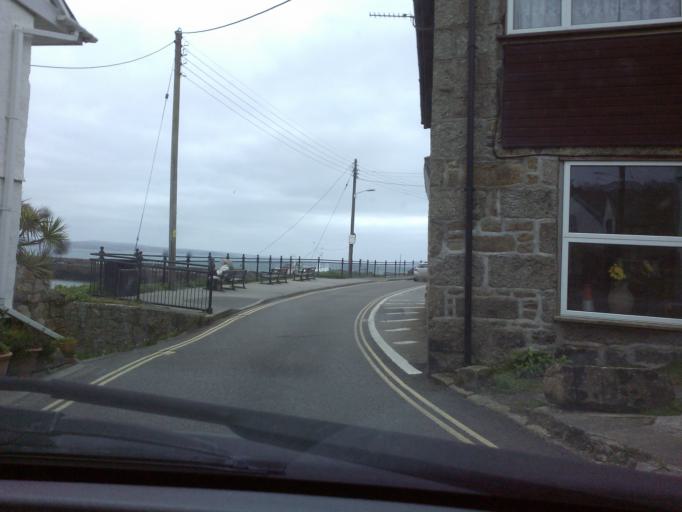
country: GB
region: England
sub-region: Cornwall
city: Penzance
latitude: 50.1020
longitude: -5.5473
